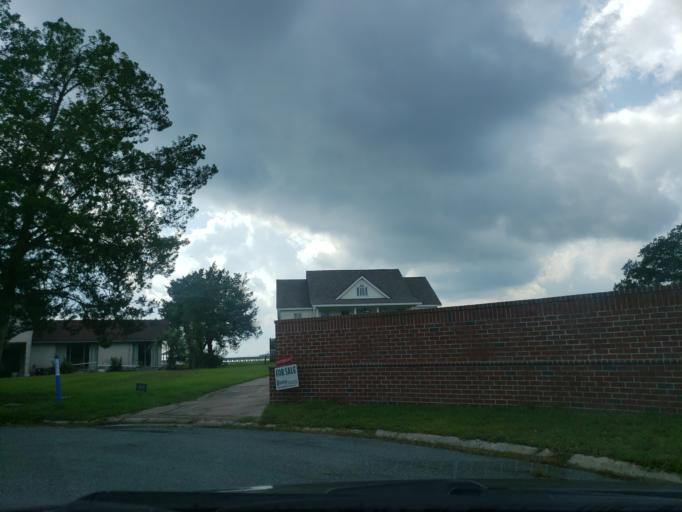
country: US
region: Georgia
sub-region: Chatham County
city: Montgomery
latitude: 31.9274
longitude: -81.0895
